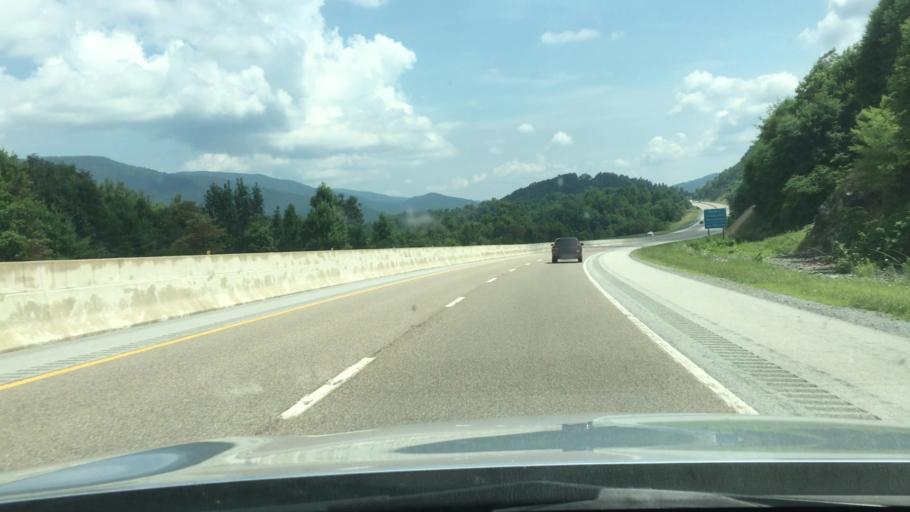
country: US
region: Tennessee
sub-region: Unicoi County
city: Banner Hill
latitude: 36.0324
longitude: -82.5394
